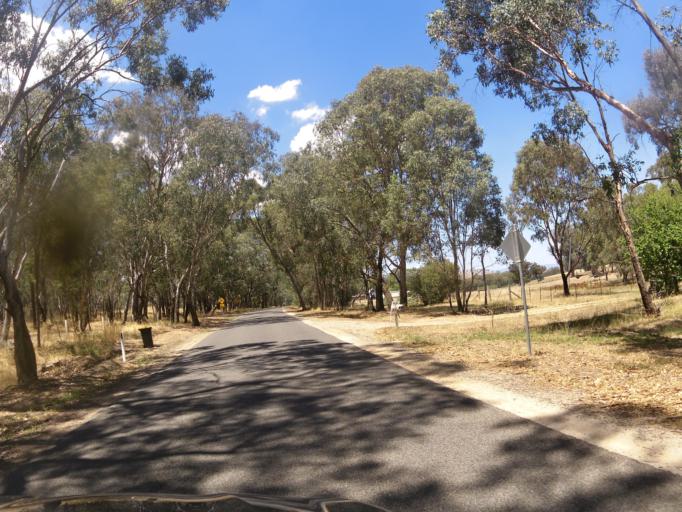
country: AU
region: Victoria
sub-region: Wangaratta
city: Wangaratta
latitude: -36.4063
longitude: 146.5450
